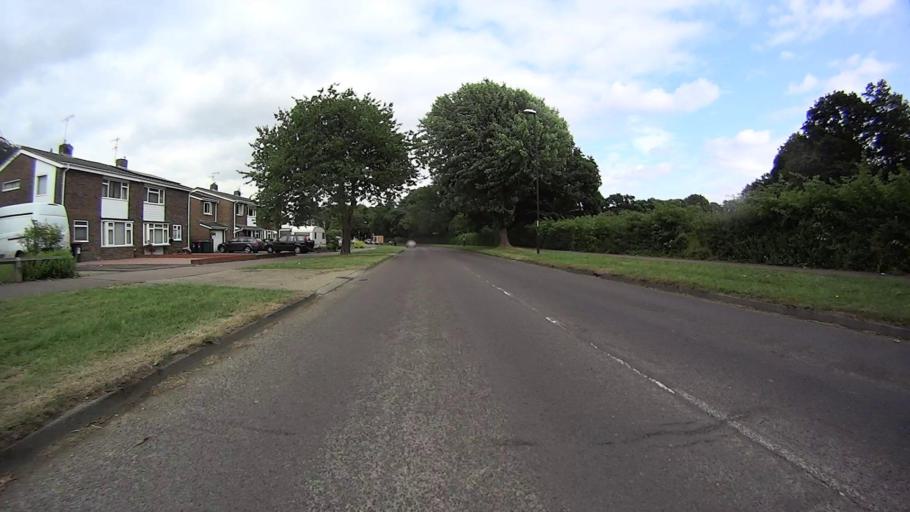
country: GB
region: England
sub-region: West Sussex
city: Langley Green
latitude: 51.1224
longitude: -0.2022
